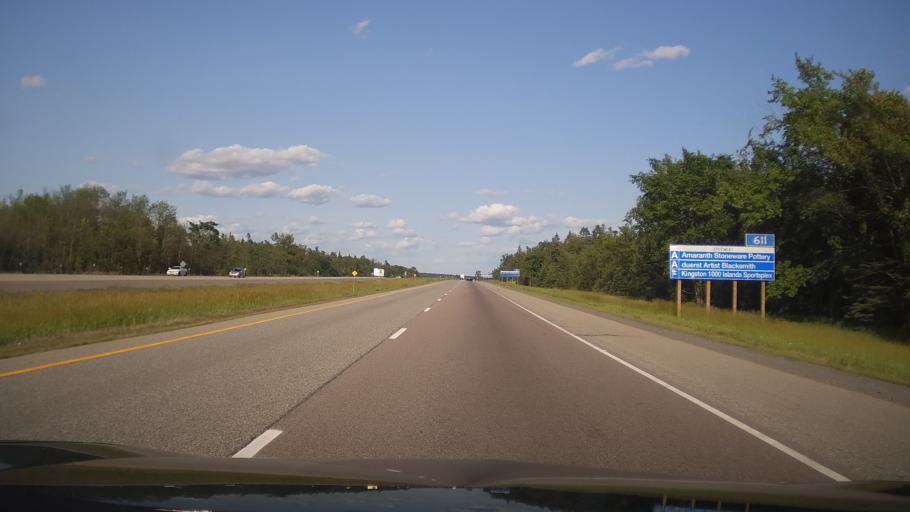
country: CA
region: Ontario
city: Kingston
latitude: 44.2872
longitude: -76.6061
